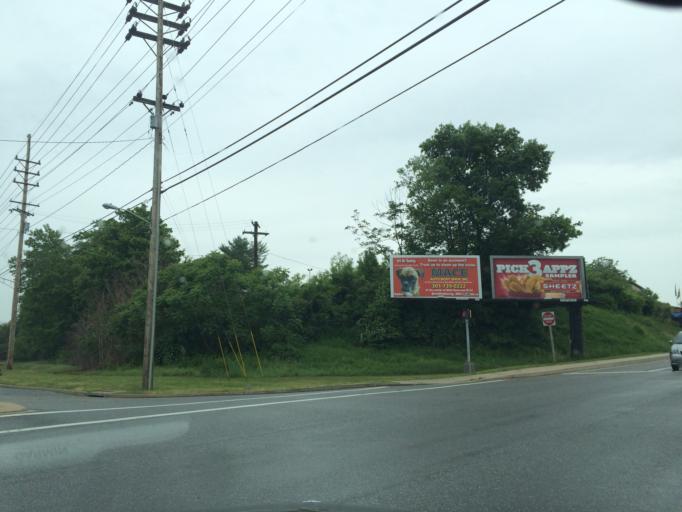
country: US
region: Maryland
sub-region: Washington County
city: Hagerstown
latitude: 39.6316
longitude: -77.7018
